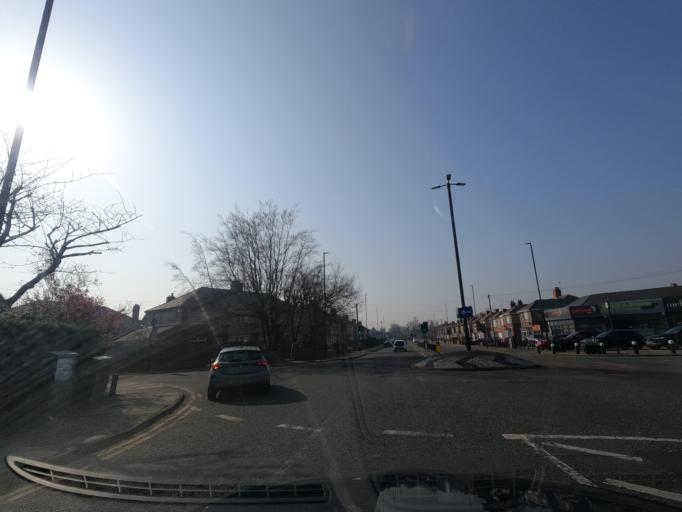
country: GB
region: England
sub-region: Newcastle upon Tyne
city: Gosforth
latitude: 54.9998
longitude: -1.5802
